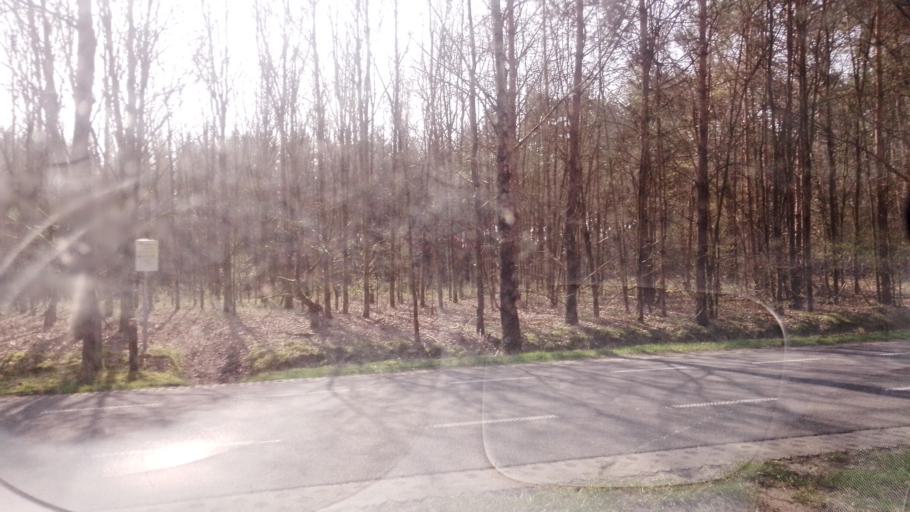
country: NL
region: Limburg
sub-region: Gemeente Peel en Maas
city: Maasbree
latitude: 51.3972
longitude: 5.9968
